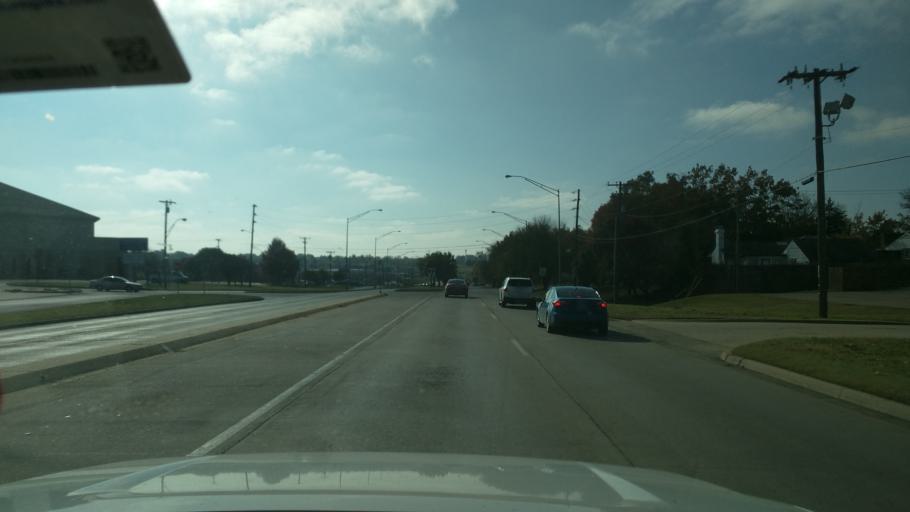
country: US
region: Oklahoma
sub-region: Washington County
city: Dewey
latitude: 36.7541
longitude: -95.9356
